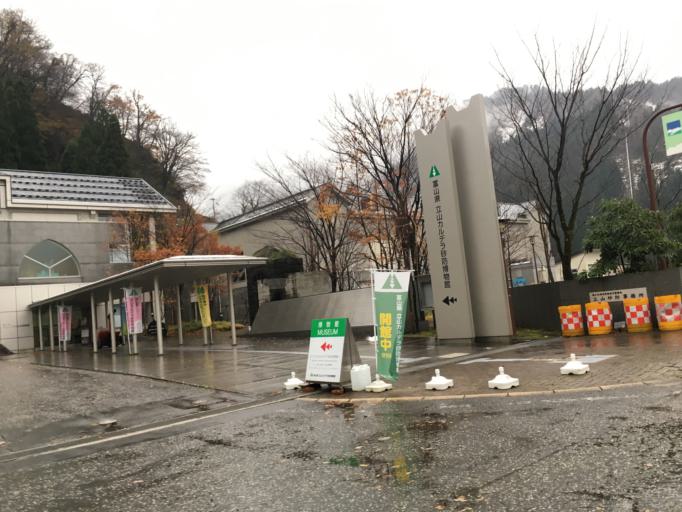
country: JP
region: Toyama
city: Kamiichi
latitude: 36.5823
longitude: 137.4454
